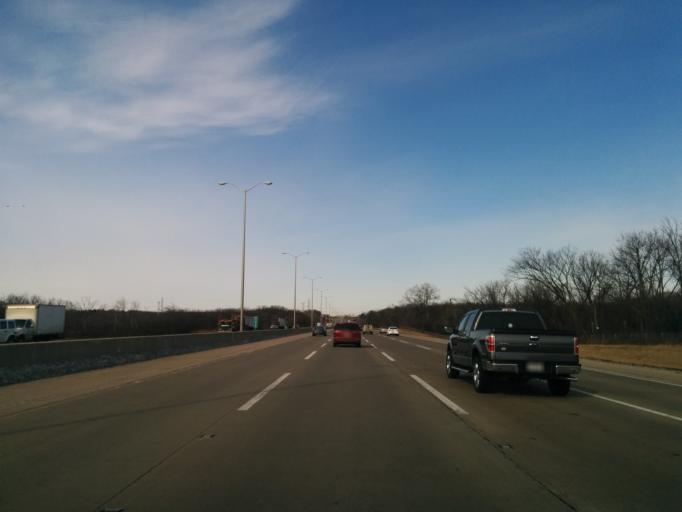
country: US
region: Illinois
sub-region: Lake County
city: Gurnee
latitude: 42.3475
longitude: -87.9251
